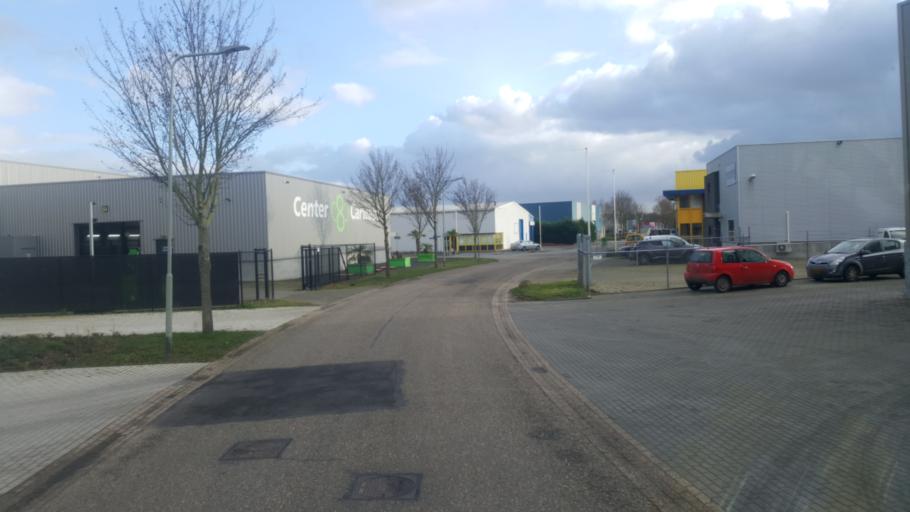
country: NL
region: Limburg
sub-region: Gemeente Venlo
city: Tegelen
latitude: 51.3214
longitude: 6.1245
